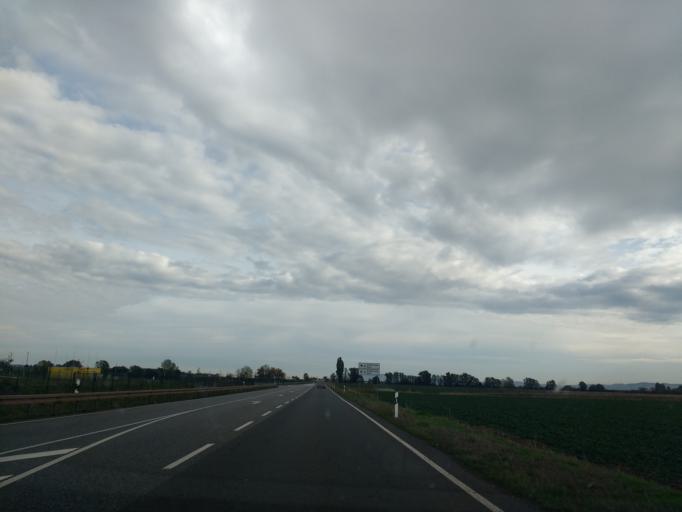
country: DE
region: Thuringia
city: Heringen
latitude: 51.4809
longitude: 10.8608
